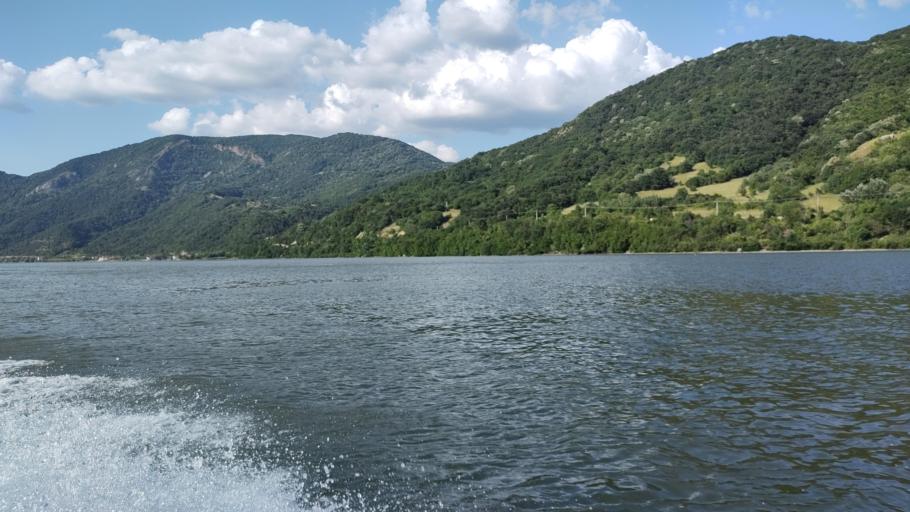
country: RO
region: Mehedinti
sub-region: Comuna Svinita
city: Svinita
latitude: 44.5713
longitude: 22.0284
